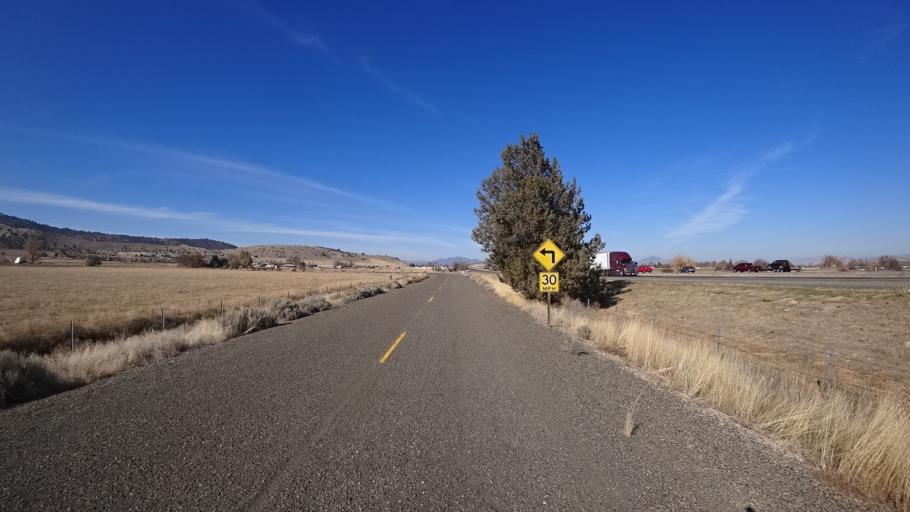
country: US
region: California
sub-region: Siskiyou County
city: Montague
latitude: 41.6313
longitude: -122.5253
